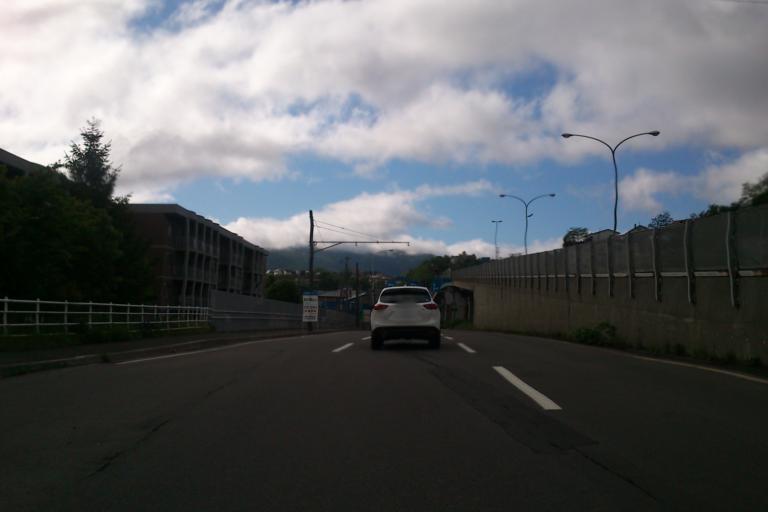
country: JP
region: Hokkaido
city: Otaru
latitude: 43.1827
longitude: 141.0188
